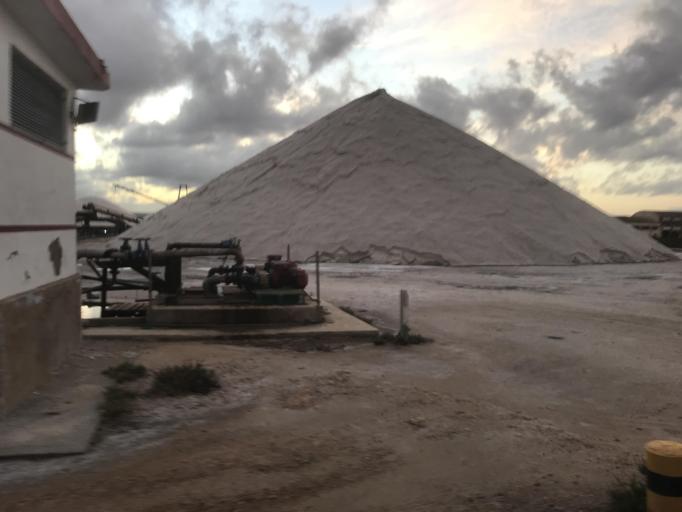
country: ES
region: Valencia
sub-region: Provincia de Alicante
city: Torrevieja
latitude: 37.9803
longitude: -0.6990
